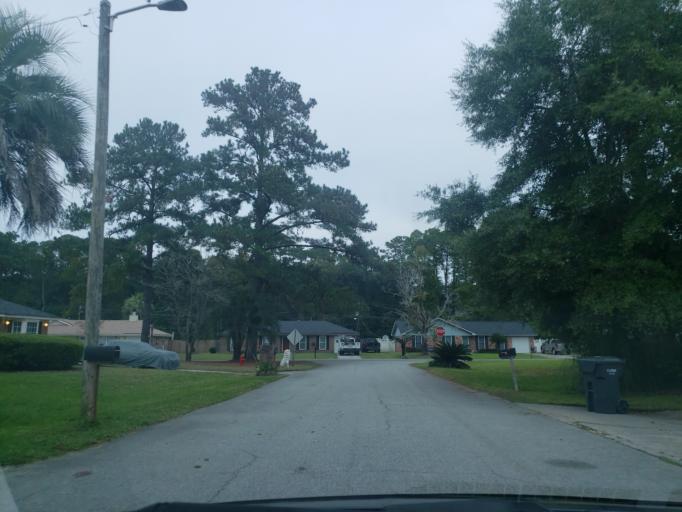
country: US
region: Georgia
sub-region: Chatham County
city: Montgomery
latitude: 31.9526
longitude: -81.1085
